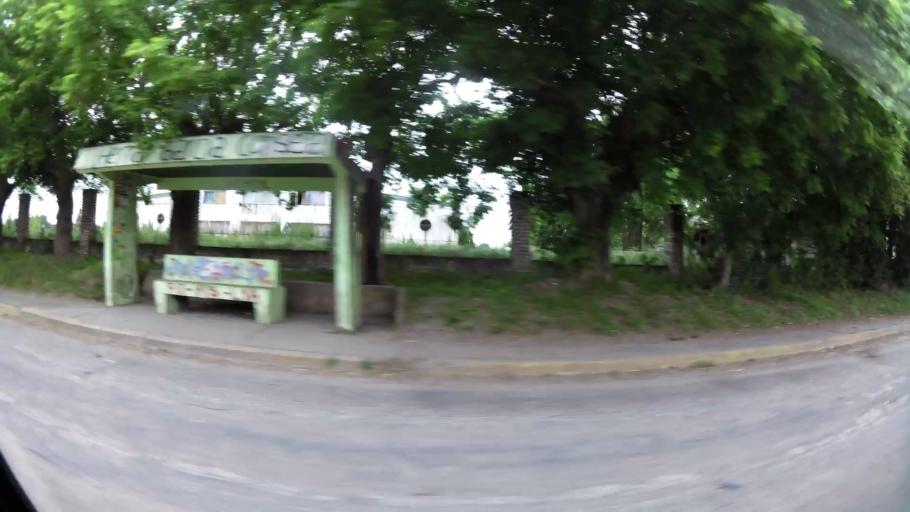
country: AR
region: Buenos Aires
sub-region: Partido de La Plata
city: La Plata
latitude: -34.9726
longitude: -58.0231
